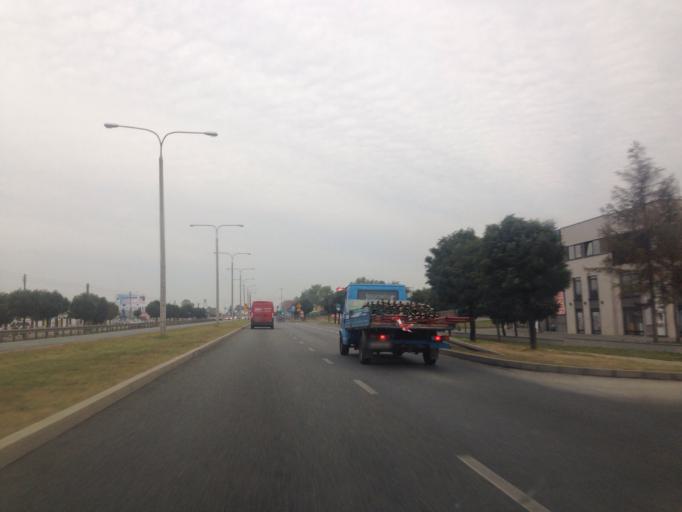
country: PL
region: Greater Poland Voivodeship
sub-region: Powiat gnieznienski
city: Gniezno
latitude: 52.5322
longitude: 17.5552
